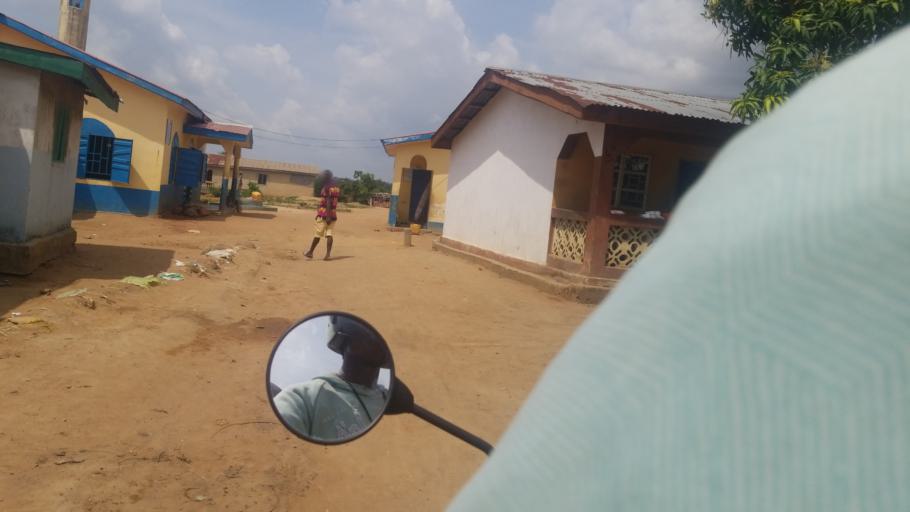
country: SL
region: Western Area
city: Waterloo
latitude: 8.3198
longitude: -13.0438
